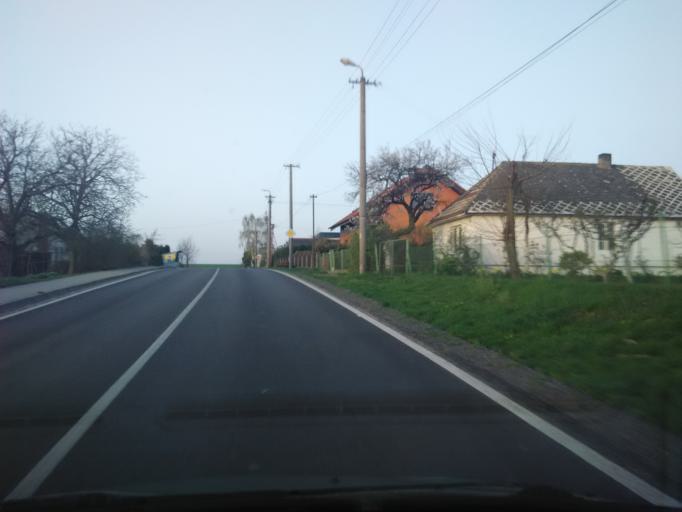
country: SK
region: Nitriansky
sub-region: Okres Nitra
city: Nitra
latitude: 48.2429
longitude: 18.0164
